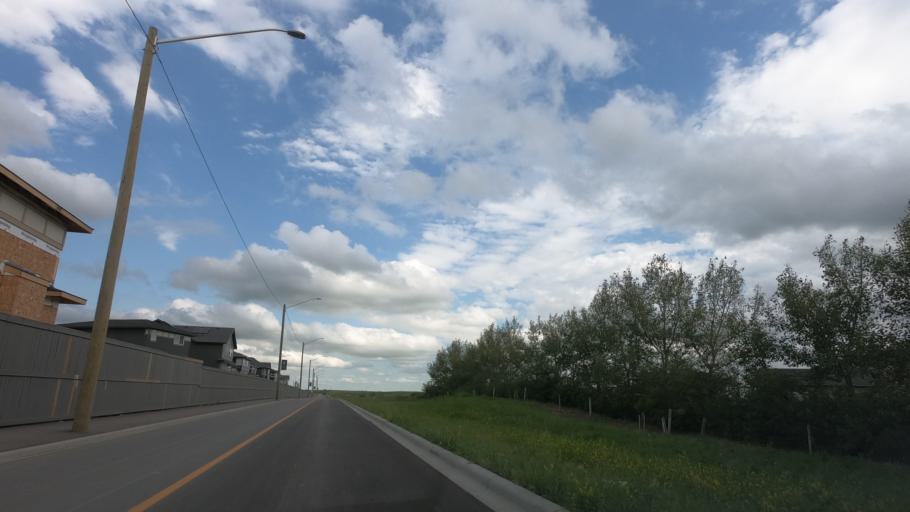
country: CA
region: Alberta
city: Airdrie
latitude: 51.2564
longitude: -113.9866
